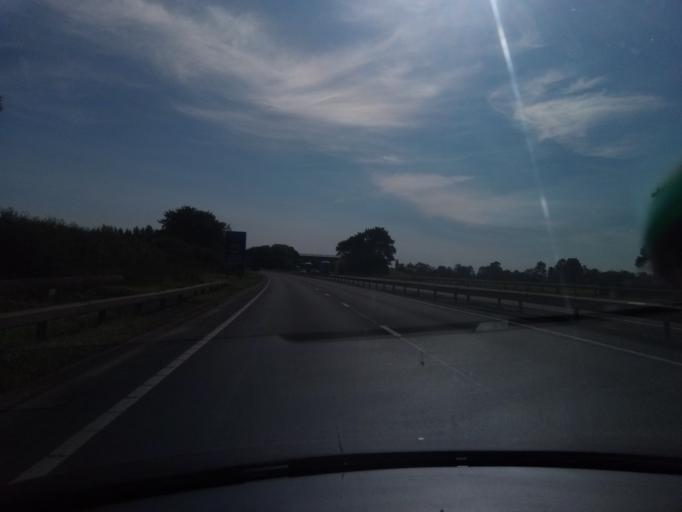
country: GB
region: England
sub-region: North Yorkshire
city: Thirsk
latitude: 54.2431
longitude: -1.3334
